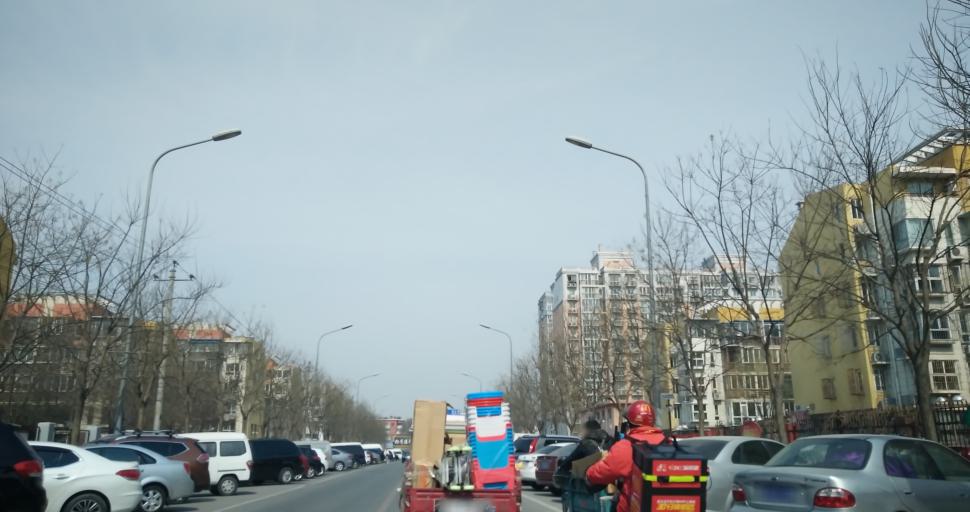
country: CN
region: Beijing
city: Jiugong
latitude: 39.8572
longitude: 116.5041
